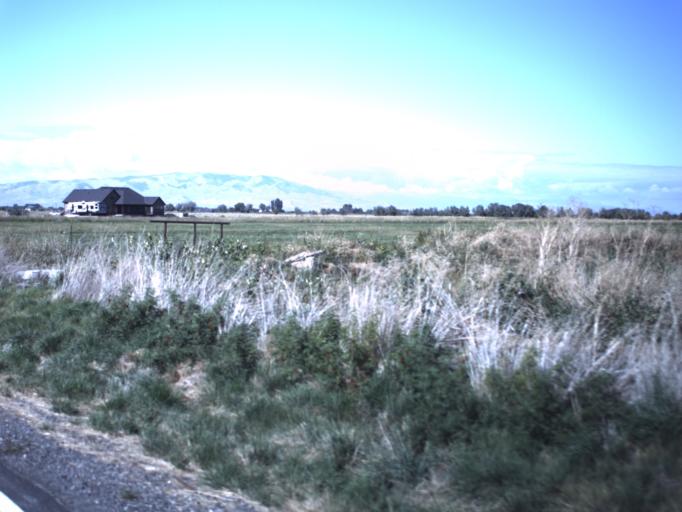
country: US
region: Utah
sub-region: Utah County
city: Spanish Fork
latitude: 40.1585
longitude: -111.6895
